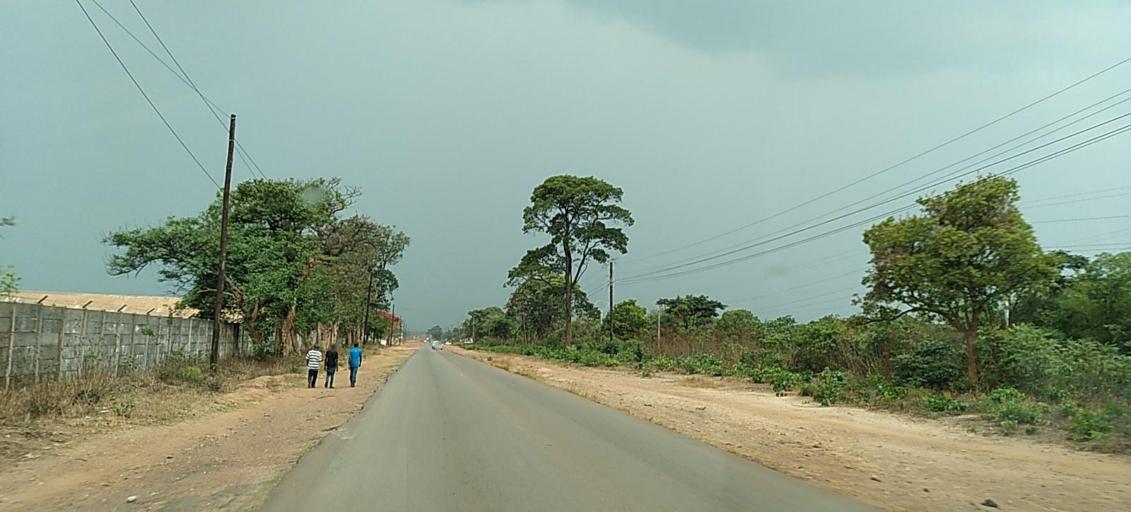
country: ZM
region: Copperbelt
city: Kalulushi
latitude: -12.8331
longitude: 28.1065
